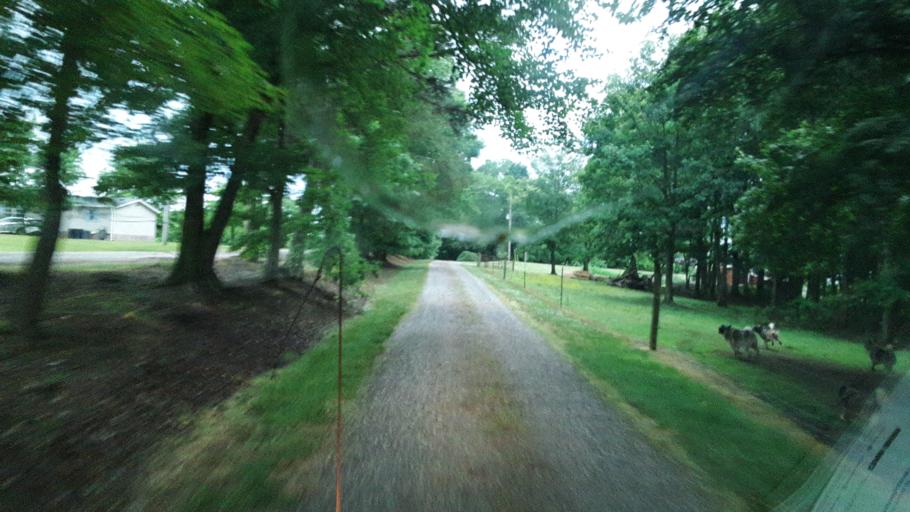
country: US
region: North Carolina
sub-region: Yadkin County
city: Jonesville
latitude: 36.1166
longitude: -80.8588
